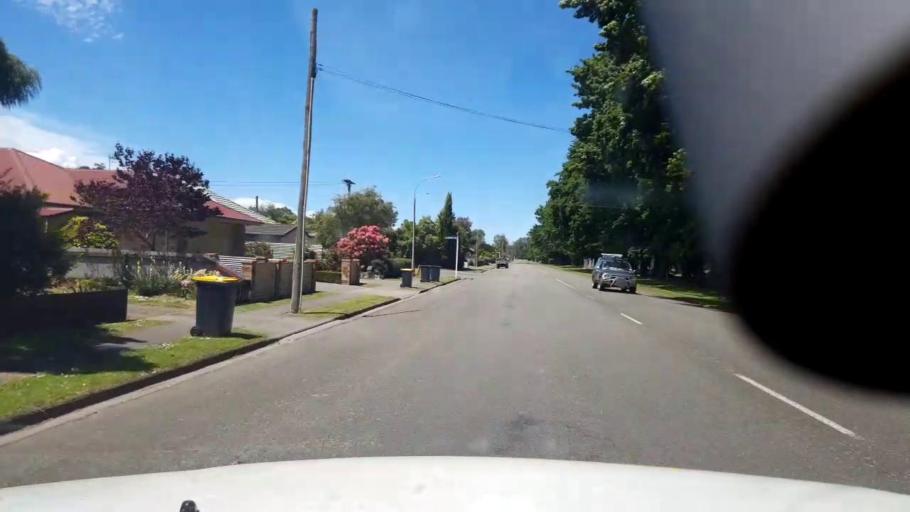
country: NZ
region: Canterbury
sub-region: Timaru District
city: Timaru
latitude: -44.2492
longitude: 171.2947
